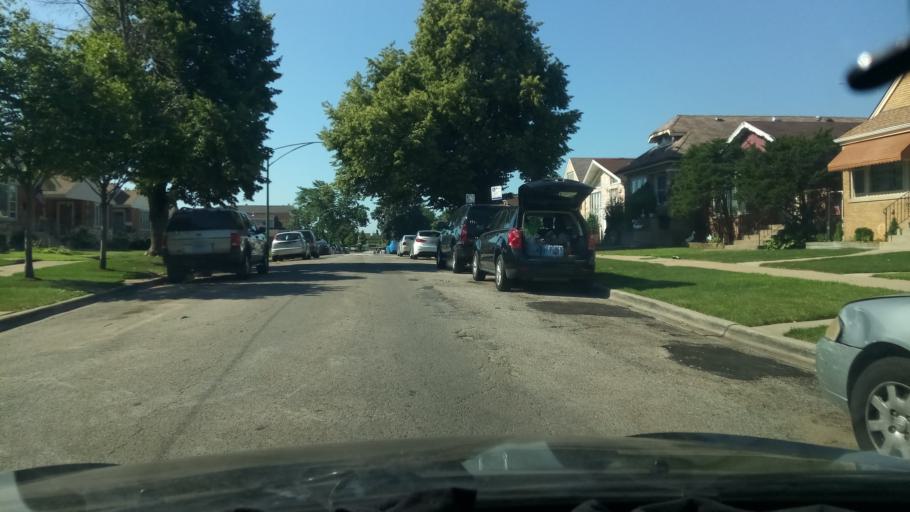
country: US
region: Illinois
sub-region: Cook County
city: Hometown
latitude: 41.7731
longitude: -87.7384
